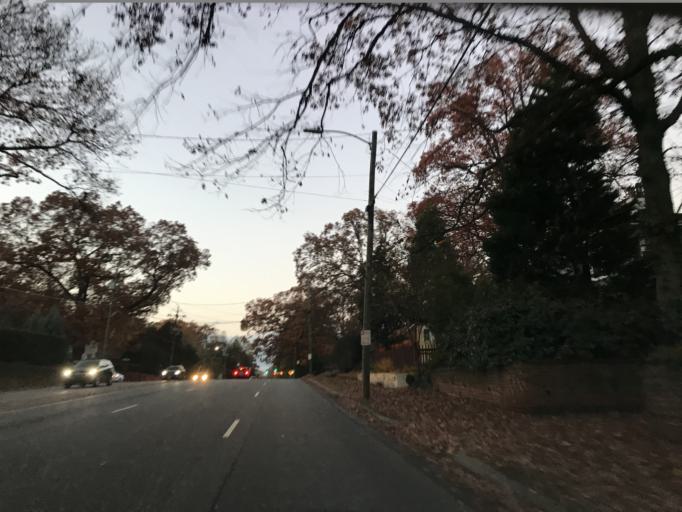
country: US
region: North Carolina
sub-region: Wake County
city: West Raleigh
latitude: 35.8106
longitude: -78.6497
